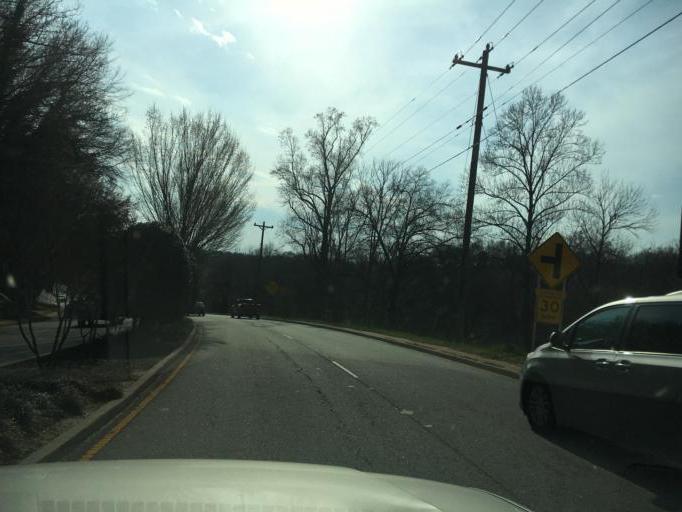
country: US
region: South Carolina
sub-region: Spartanburg County
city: Spartanburg
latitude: 34.9848
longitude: -81.9266
